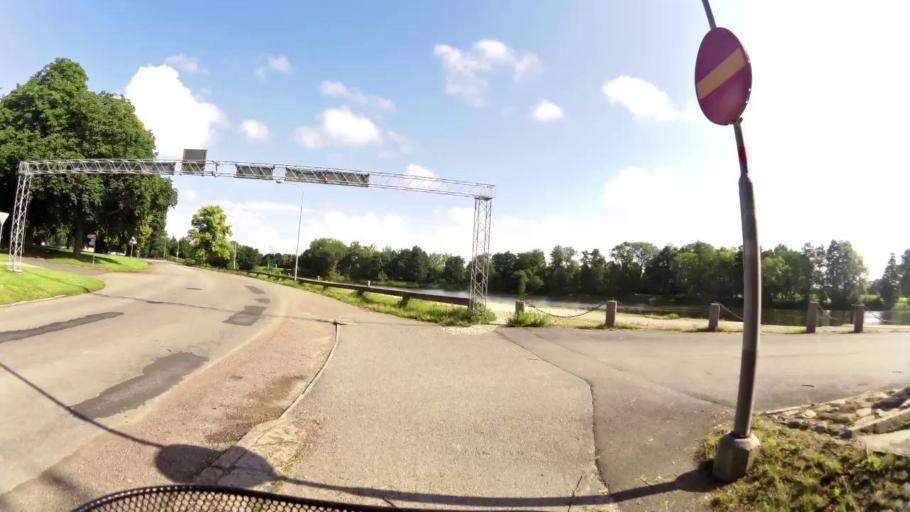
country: SE
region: OEstergoetland
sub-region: Linkopings Kommun
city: Linkoping
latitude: 58.4137
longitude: 15.6314
